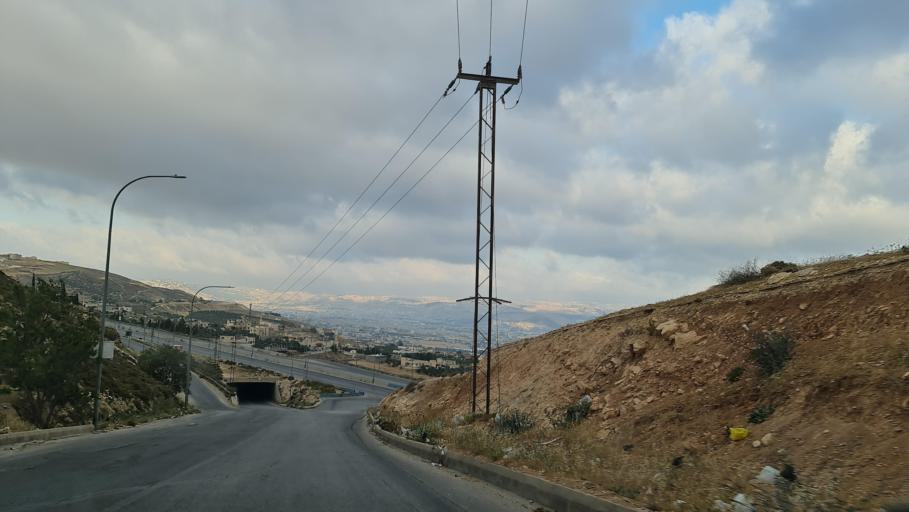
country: JO
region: Amman
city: Al Jubayhah
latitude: 32.0934
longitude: 35.8983
